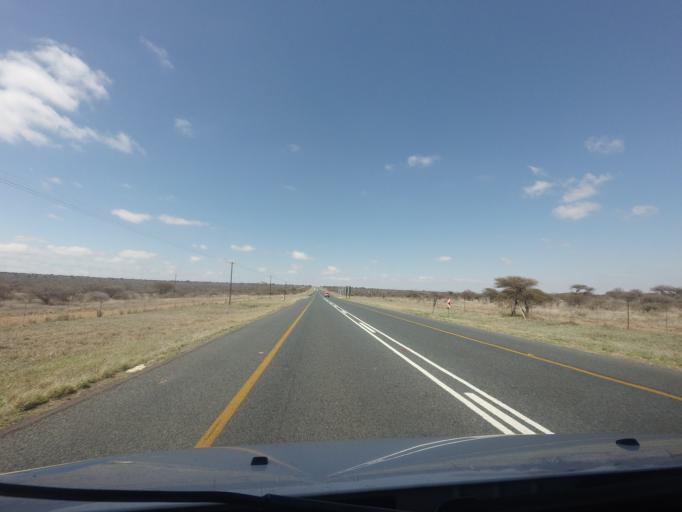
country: ZA
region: Limpopo
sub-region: Vhembe District Municipality
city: Louis Trichardt
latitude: -23.3886
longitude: 29.7639
